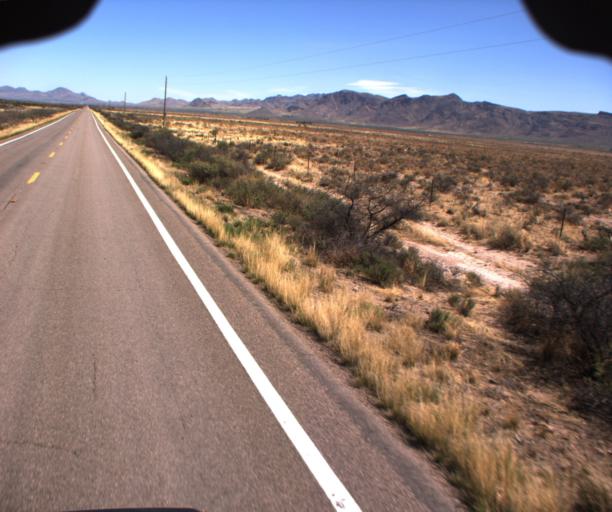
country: US
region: Arizona
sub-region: Cochise County
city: Douglas
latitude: 31.7772
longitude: -109.0726
